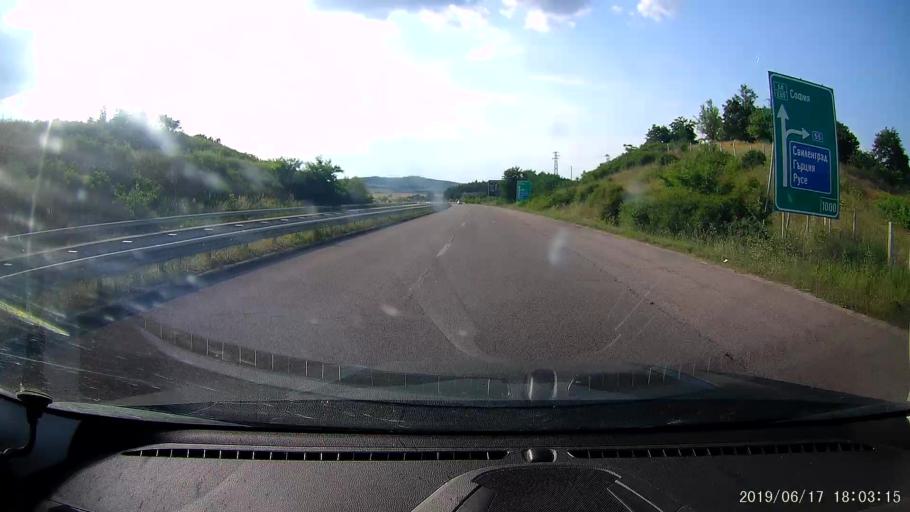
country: BG
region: Khaskovo
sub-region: Obshtina Svilengrad
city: Svilengrad
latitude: 41.7752
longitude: 26.2219
